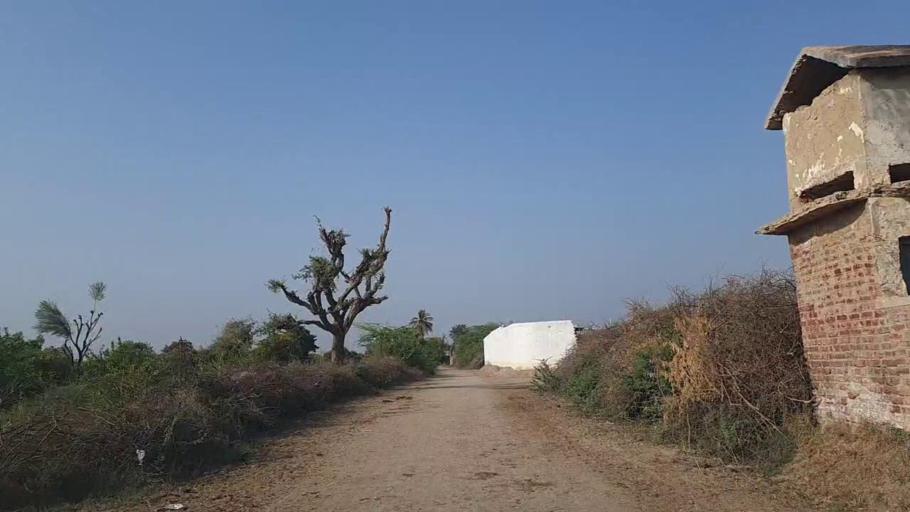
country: PK
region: Sindh
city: Dhoro Naro
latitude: 25.5092
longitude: 69.5344
